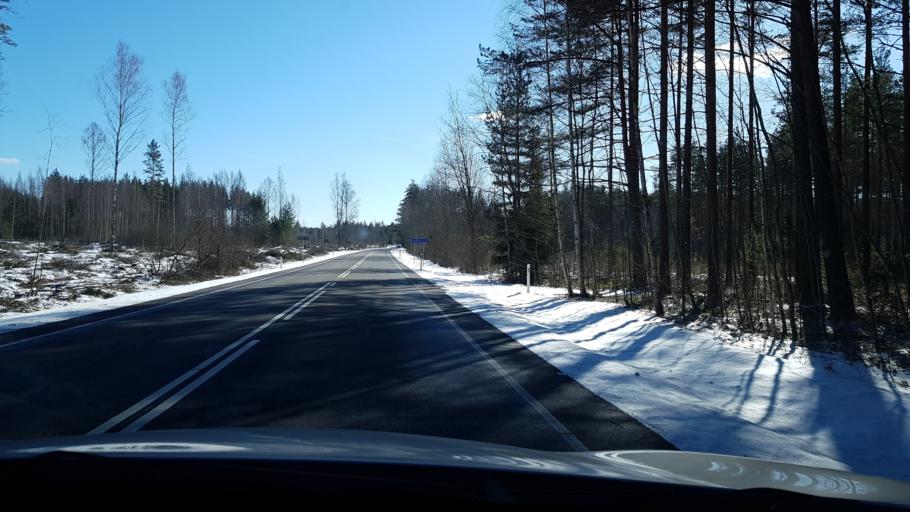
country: EE
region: Polvamaa
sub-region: Raepina vald
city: Rapina
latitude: 57.9897
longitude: 27.5635
